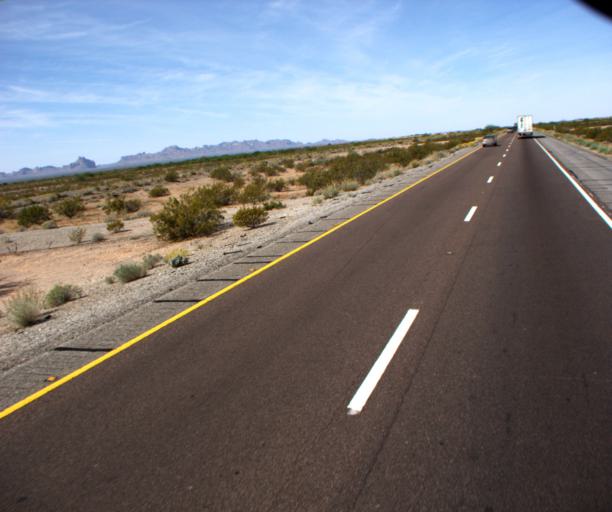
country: US
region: Arizona
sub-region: La Paz County
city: Salome
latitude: 33.5447
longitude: -113.1913
